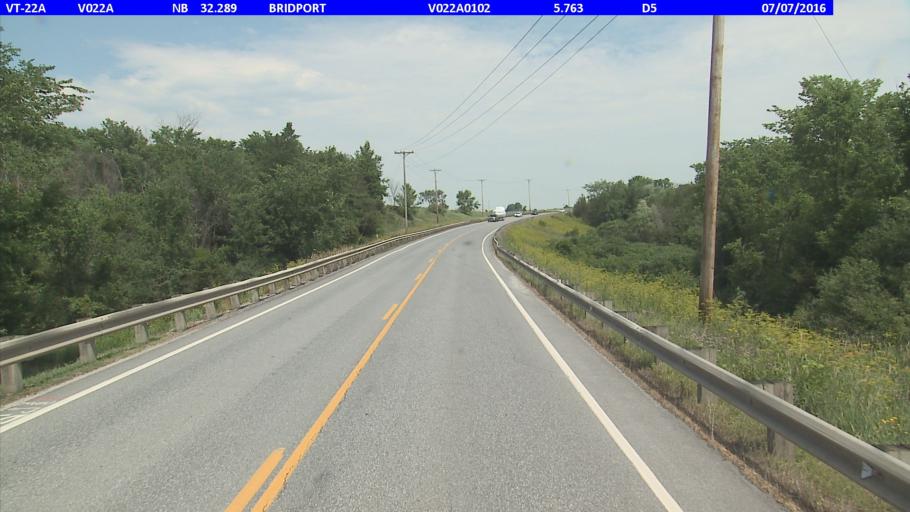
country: US
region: Vermont
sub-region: Addison County
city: Middlebury (village)
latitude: 44.0227
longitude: -73.3111
